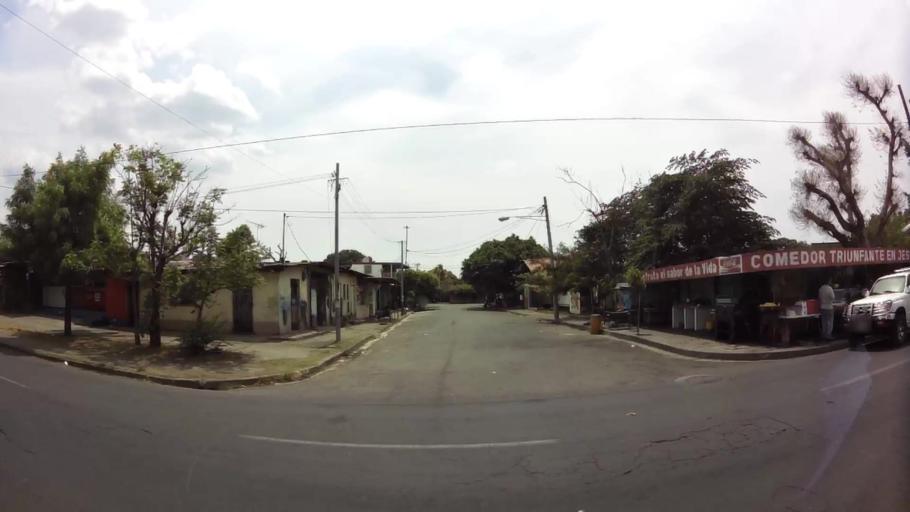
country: NI
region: Managua
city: Managua
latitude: 12.1541
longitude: -86.2825
